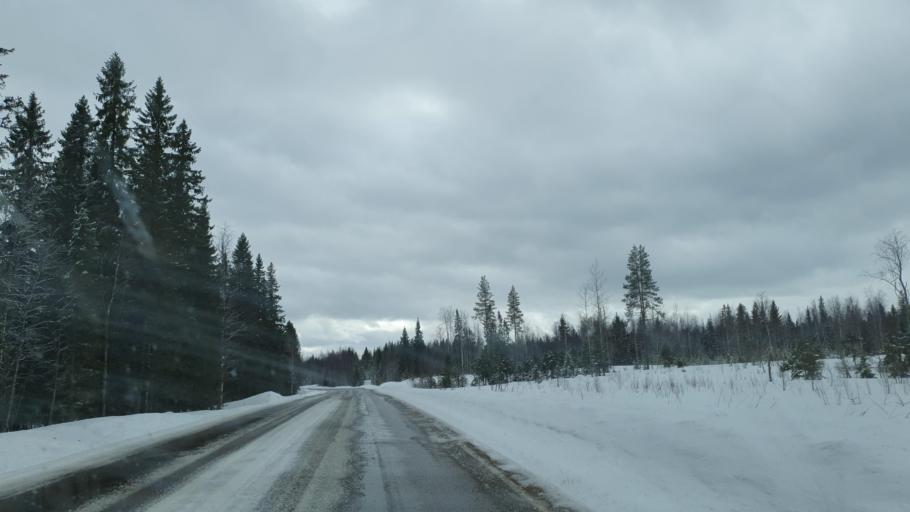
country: FI
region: Kainuu
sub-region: Kehys-Kainuu
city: Puolanka
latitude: 65.0851
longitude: 27.6998
